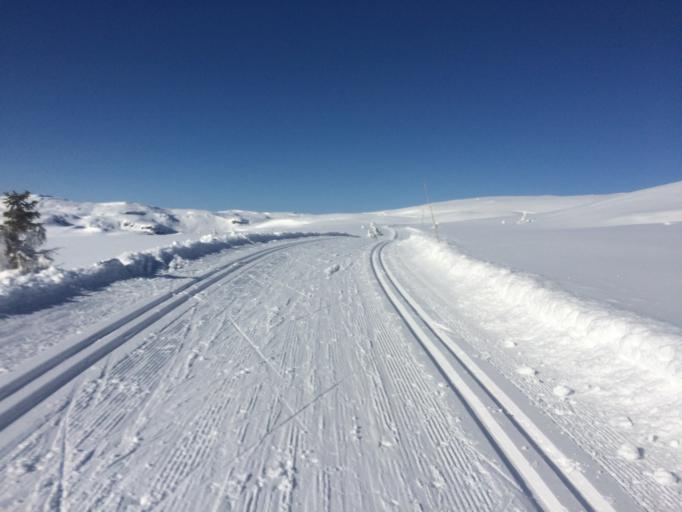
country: NO
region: Oppland
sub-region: Ringebu
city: Ringebu
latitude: 61.3668
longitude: 10.0755
